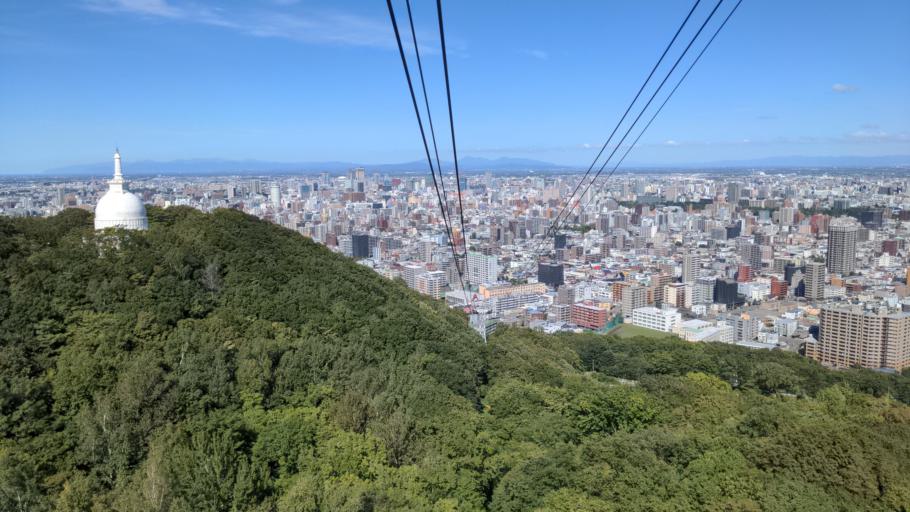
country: JP
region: Hokkaido
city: Sapporo
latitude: 43.0283
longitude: 141.3304
